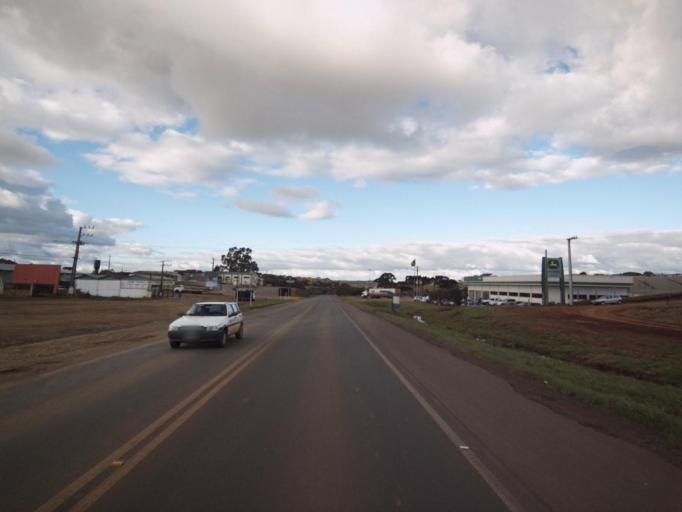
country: BR
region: Santa Catarina
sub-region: Campos Novos
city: Campos Novos
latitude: -27.3893
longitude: -51.2110
